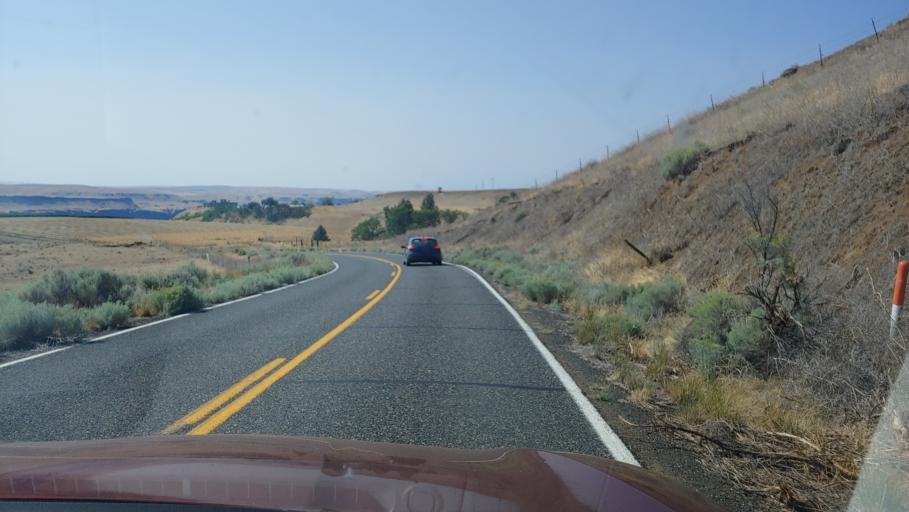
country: US
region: Washington
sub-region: Klickitat County
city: Goldendale
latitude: 45.7006
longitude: -120.7998
